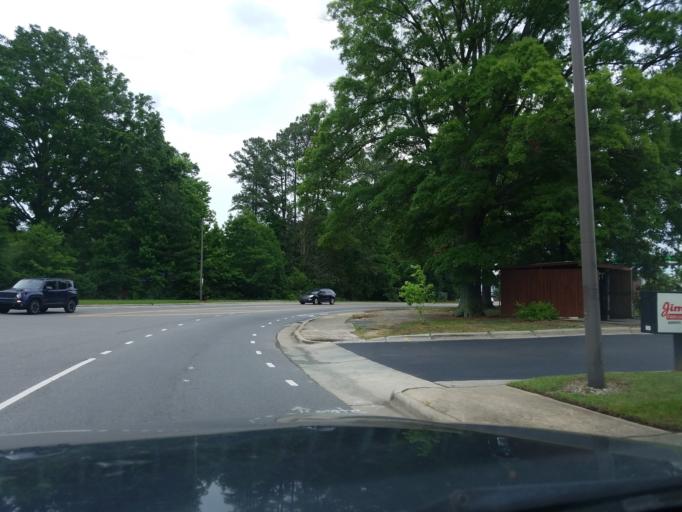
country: US
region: North Carolina
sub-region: Durham County
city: Durham
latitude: 36.0309
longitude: -78.9275
